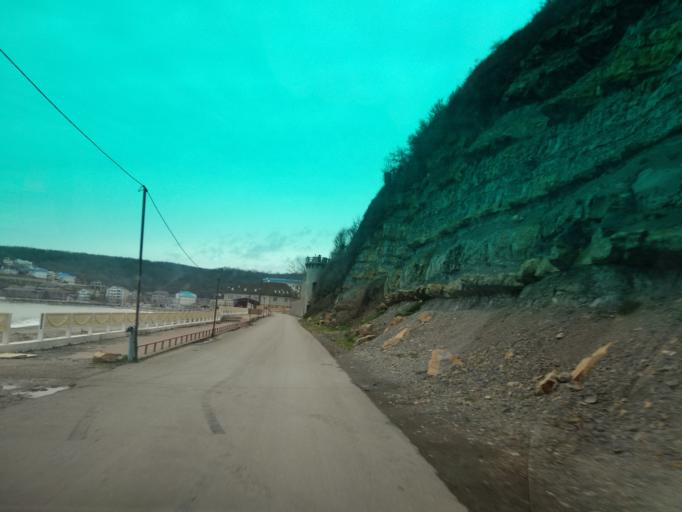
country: RU
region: Krasnodarskiy
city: Novomikhaylovskiy
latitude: 44.2368
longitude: 38.8381
